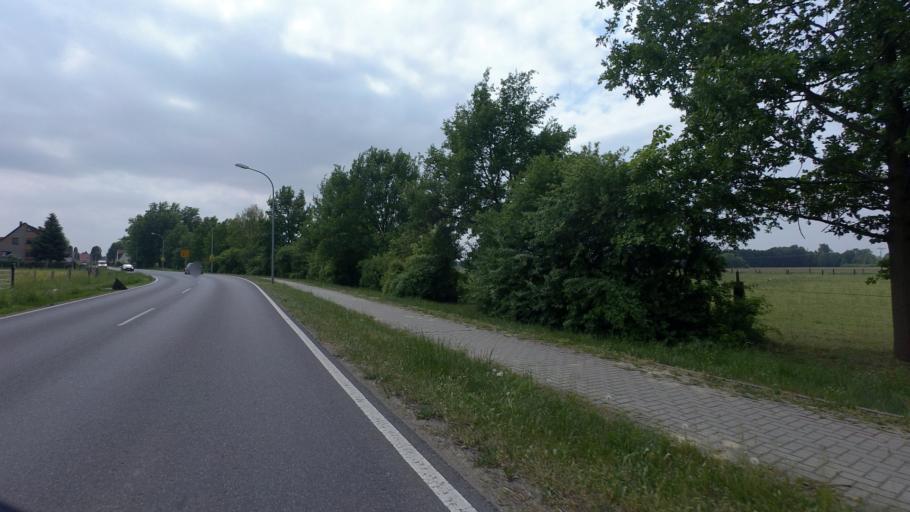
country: DE
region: Brandenburg
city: Drehnow
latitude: 51.8723
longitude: 14.3782
